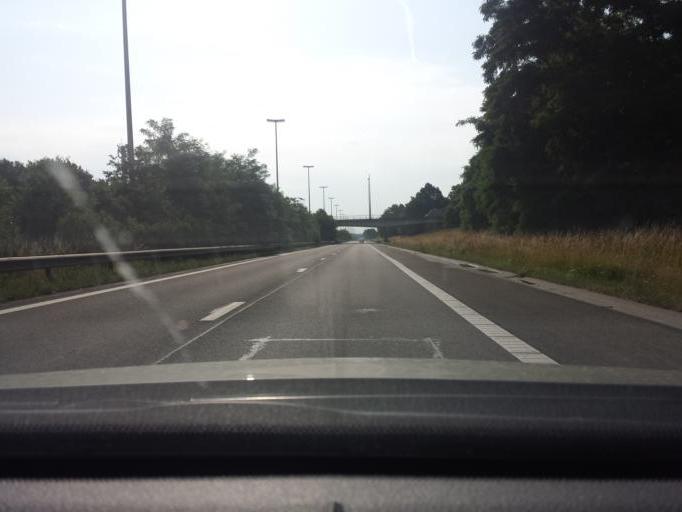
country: BE
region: Flanders
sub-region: Provincie Limburg
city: Diepenbeek
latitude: 50.8932
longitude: 5.4155
